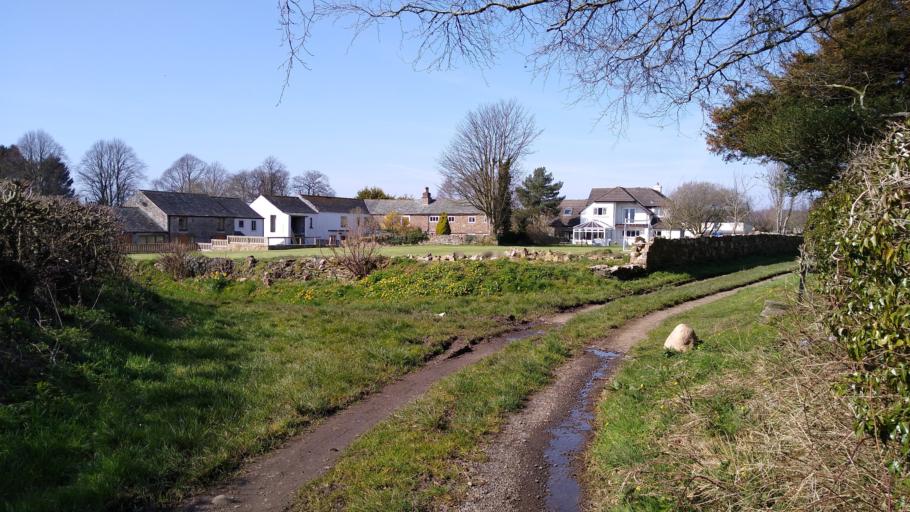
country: GB
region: England
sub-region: Cumbria
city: Dearham
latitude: 54.6737
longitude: -3.4262
